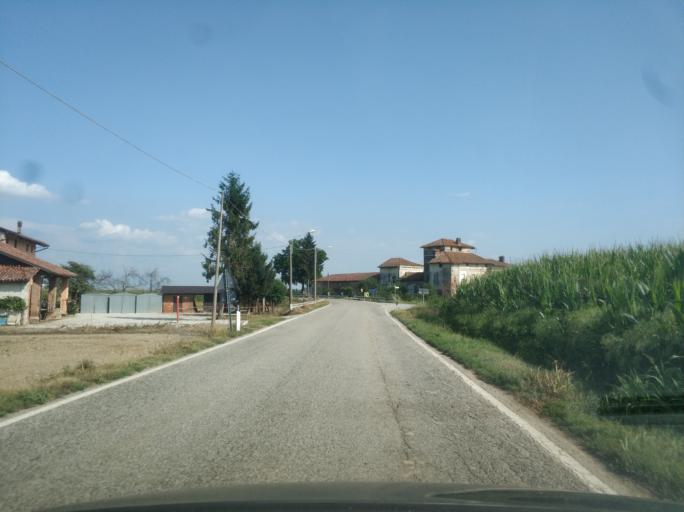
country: IT
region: Piedmont
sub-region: Provincia di Cuneo
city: Centallo
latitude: 44.5340
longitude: 7.6274
